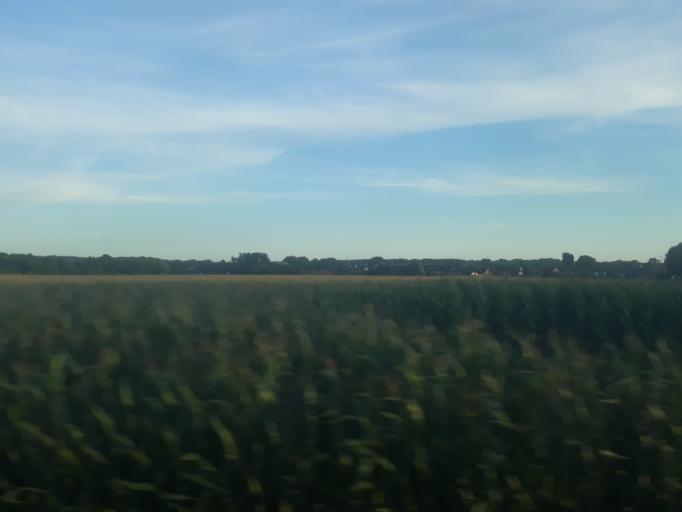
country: DE
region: Lower Saxony
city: Neu Wulmstorf
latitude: 53.4737
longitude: 9.8016
